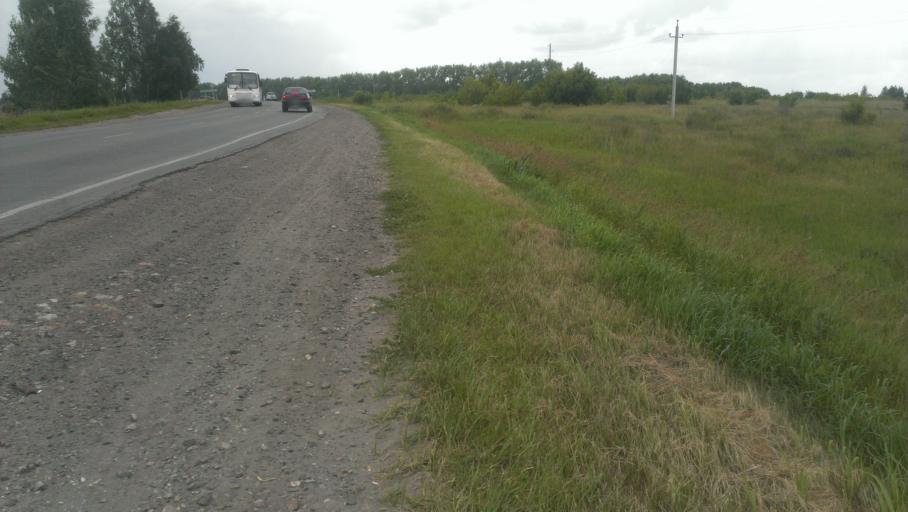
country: RU
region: Altai Krai
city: Gon'ba
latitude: 53.3905
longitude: 83.6008
